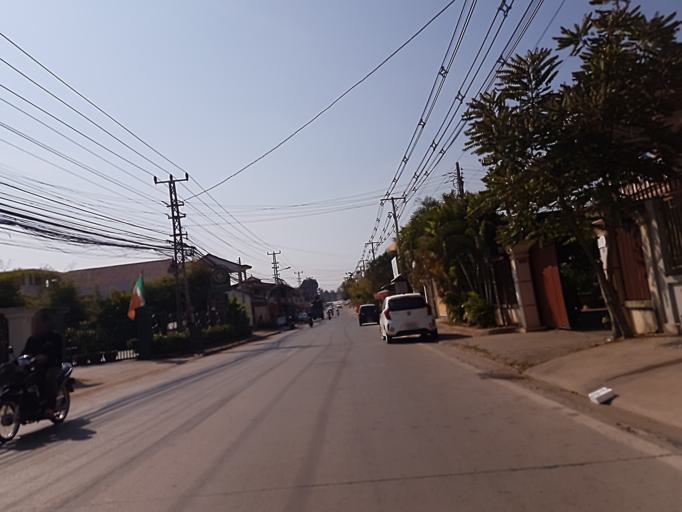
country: LA
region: Vientiane
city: Vientiane
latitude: 17.9449
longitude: 102.6364
